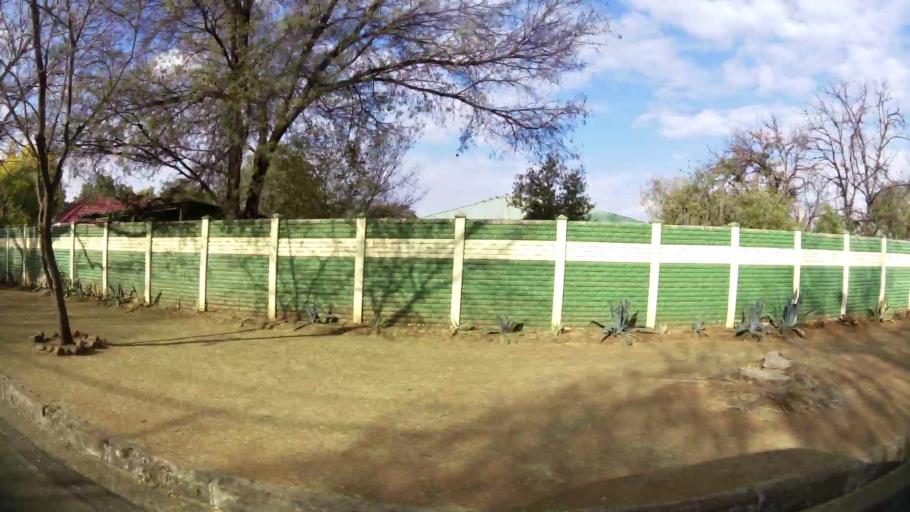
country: ZA
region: Orange Free State
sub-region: Mangaung Metropolitan Municipality
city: Bloemfontein
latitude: -29.0813
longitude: 26.2160
